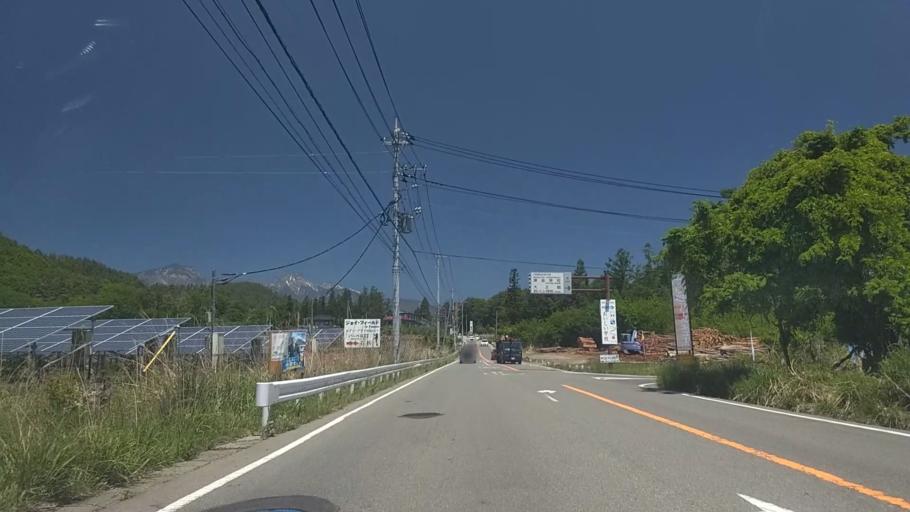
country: JP
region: Yamanashi
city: Nirasaki
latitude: 35.8512
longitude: 138.4320
